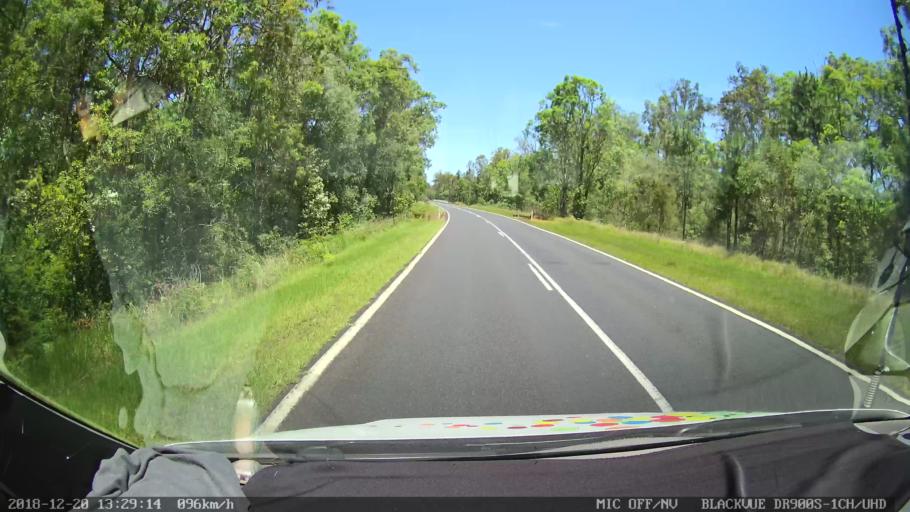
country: AU
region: New South Wales
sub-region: Clarence Valley
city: Gordon
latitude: -29.1863
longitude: 152.9888
